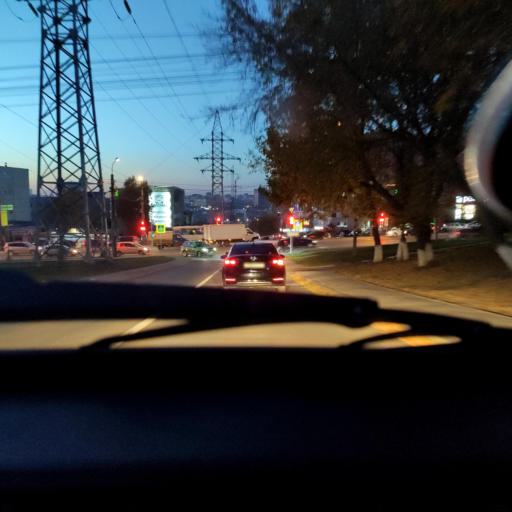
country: RU
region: Bashkortostan
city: Ufa
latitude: 54.7111
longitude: 55.9900
